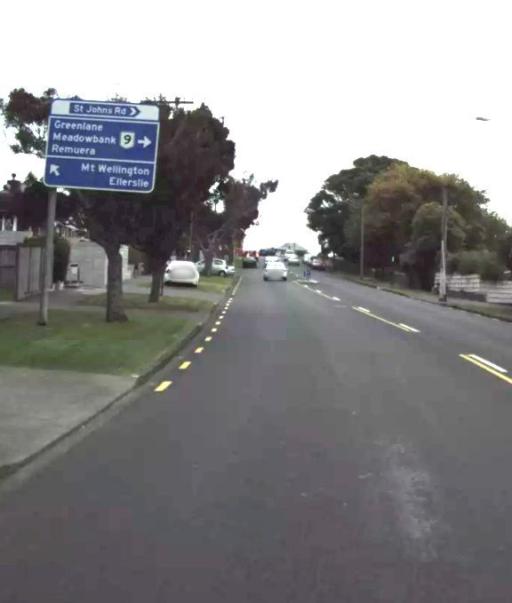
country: NZ
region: Auckland
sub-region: Auckland
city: Tamaki
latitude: -36.8727
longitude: 174.8435
